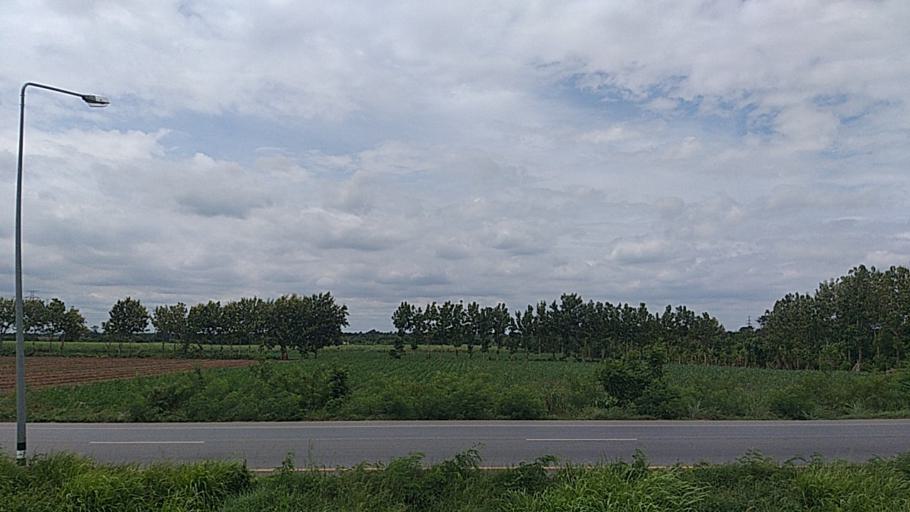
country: TH
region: Nakhon Ratchasima
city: Sung Noen
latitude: 14.8329
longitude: 101.7841
